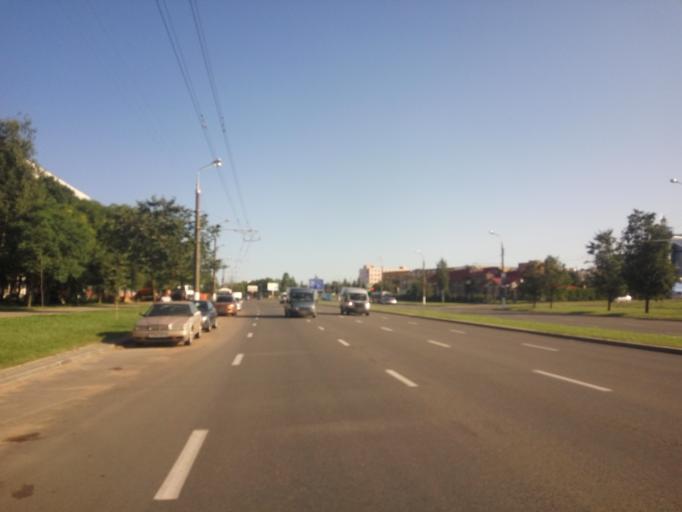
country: BY
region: Vitebsk
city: Vitebsk
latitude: 55.1894
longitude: 30.2495
